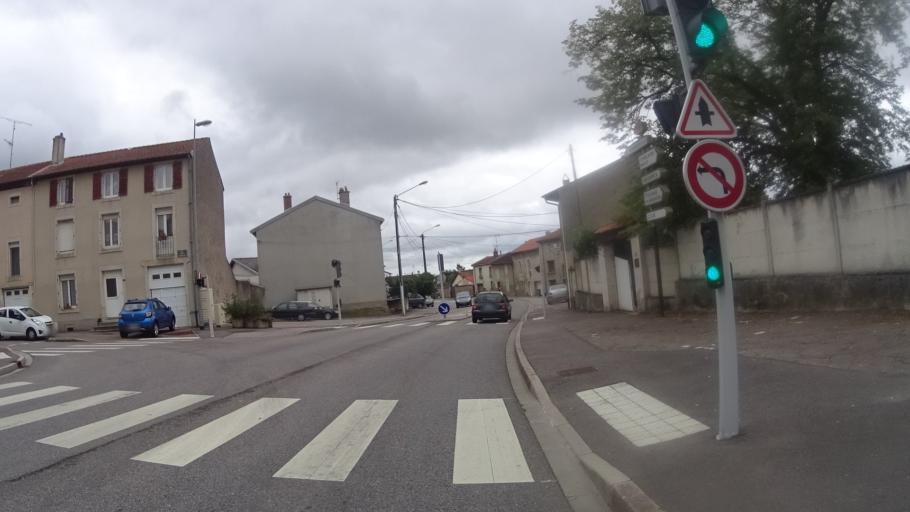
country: FR
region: Lorraine
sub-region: Departement de Meurthe-et-Moselle
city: Art-sur-Meurthe
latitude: 48.6556
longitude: 6.2647
